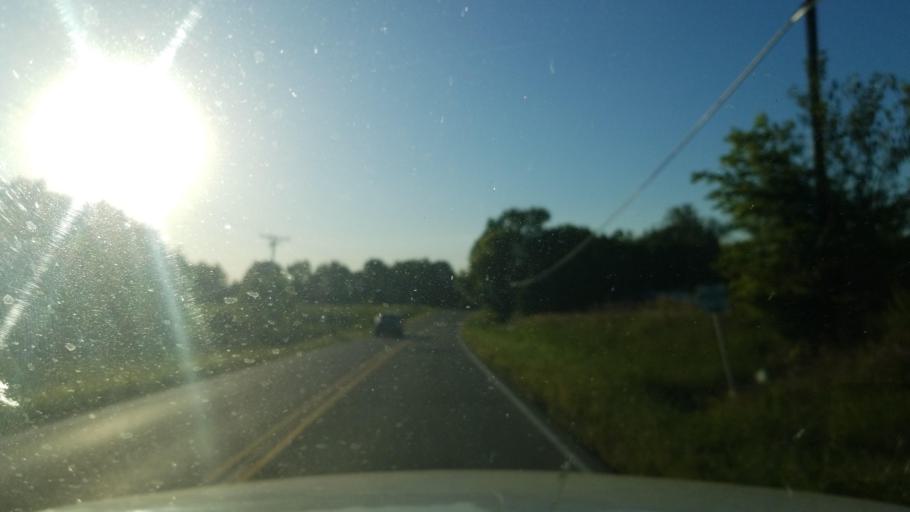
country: US
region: Illinois
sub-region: Saline County
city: Harrisburg
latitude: 37.6372
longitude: -88.5222
